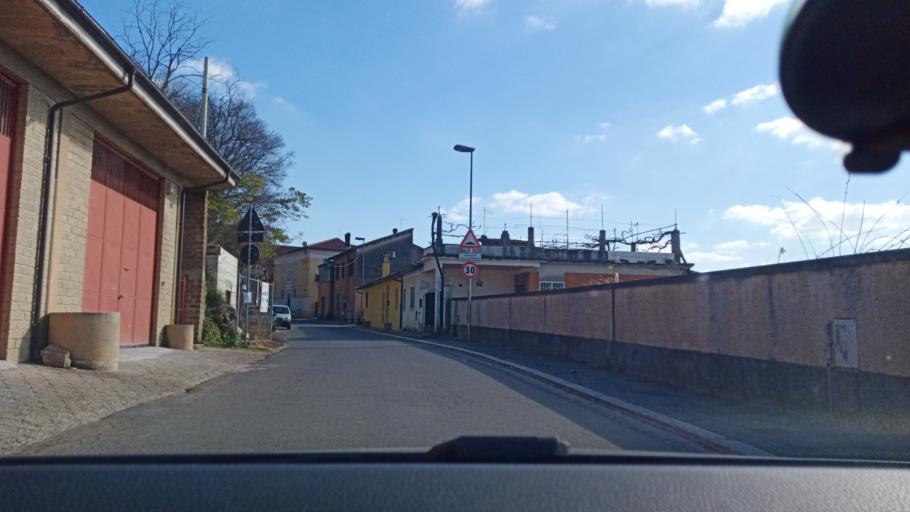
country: IT
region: Latium
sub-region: Citta metropolitana di Roma Capitale
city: Torrita Tiberina
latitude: 42.2378
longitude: 12.6154
